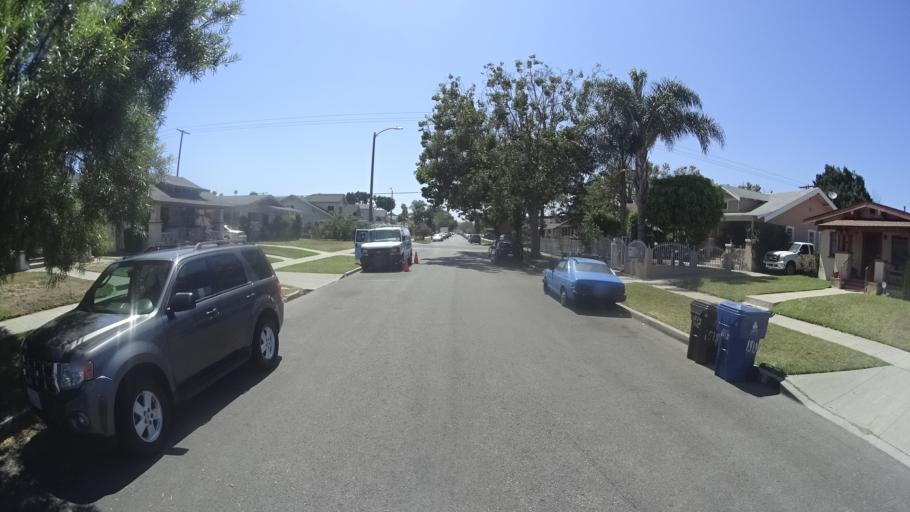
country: US
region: California
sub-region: Los Angeles County
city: View Park-Windsor Hills
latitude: 33.9991
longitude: -118.3039
